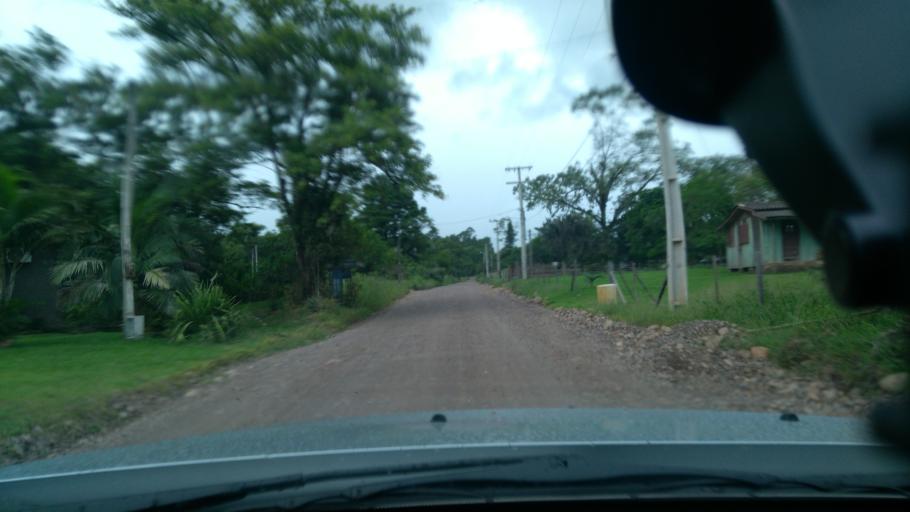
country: BR
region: Rio Grande do Sul
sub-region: Torres
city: Torres
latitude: -29.2063
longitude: -49.9739
